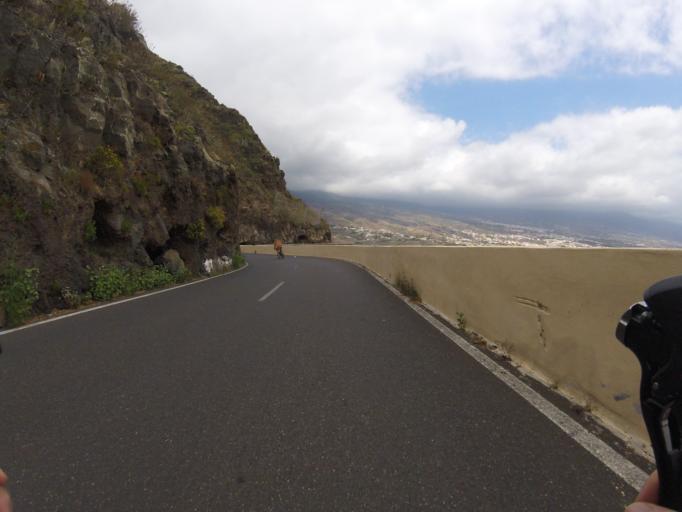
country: ES
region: Canary Islands
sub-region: Provincia de Santa Cruz de Tenerife
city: Guimar
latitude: 28.2942
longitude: -16.4087
